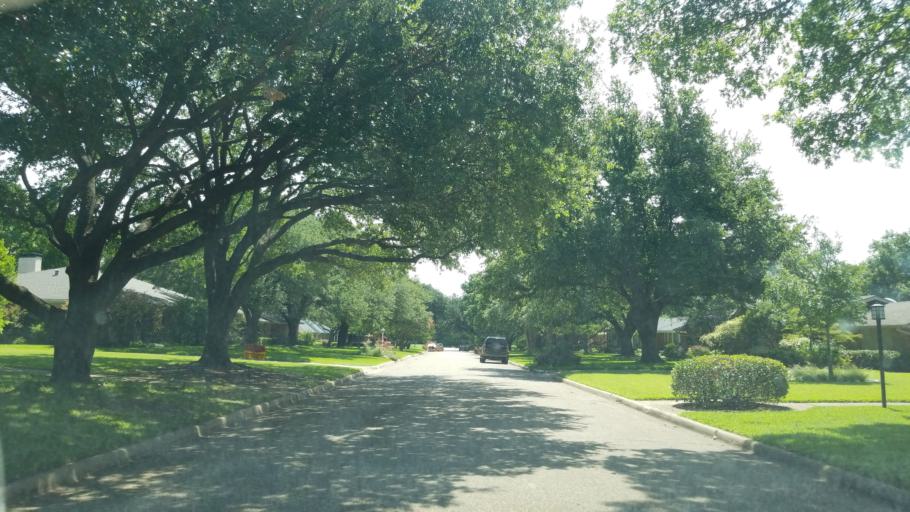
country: US
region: Texas
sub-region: Dallas County
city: Farmers Branch
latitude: 32.9080
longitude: -96.8495
